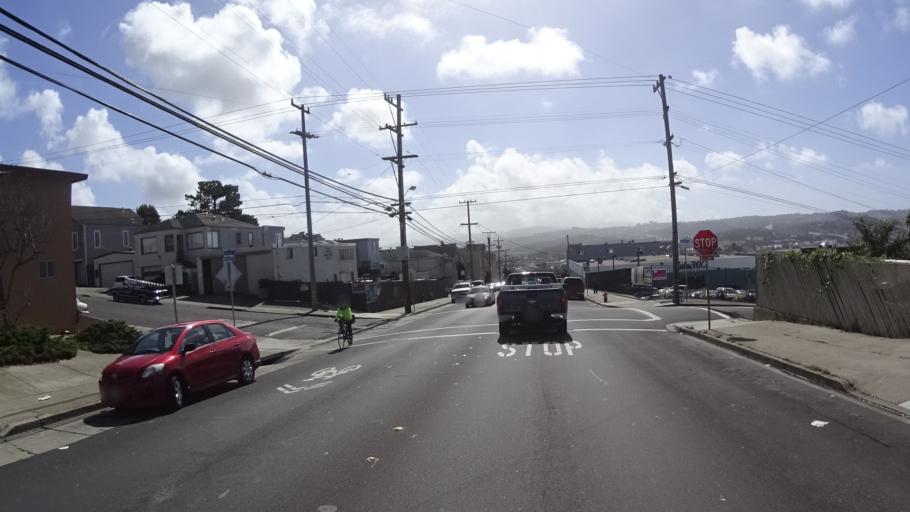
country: US
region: California
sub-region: San Mateo County
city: Daly City
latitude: 37.6962
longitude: -122.4620
